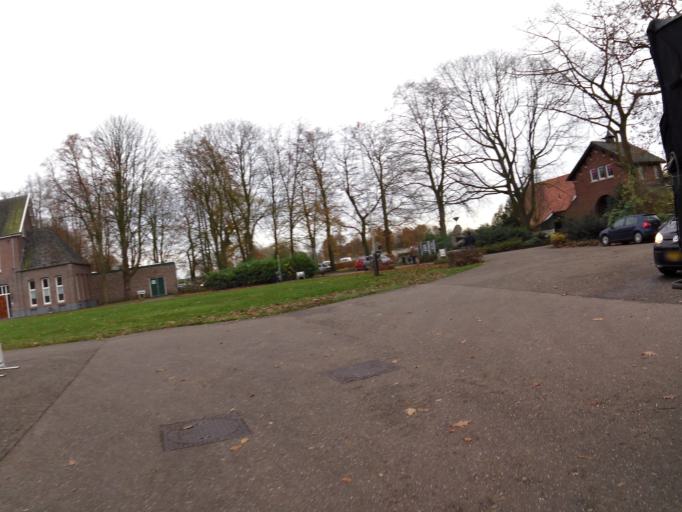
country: NL
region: North Brabant
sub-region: Gemeente Heusden
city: Heusden
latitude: 51.7020
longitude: 5.1892
